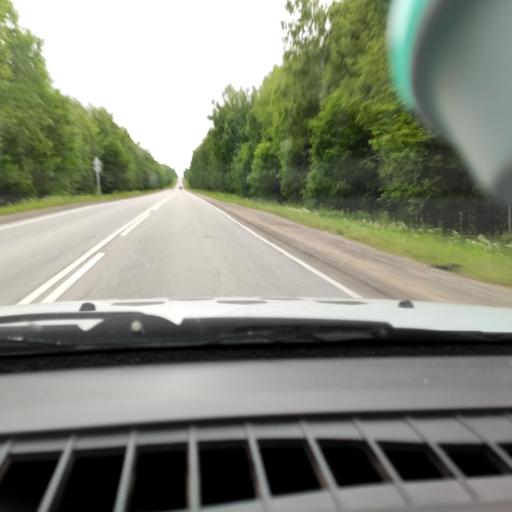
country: RU
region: Perm
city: Lys'va
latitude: 58.1511
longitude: 57.7604
